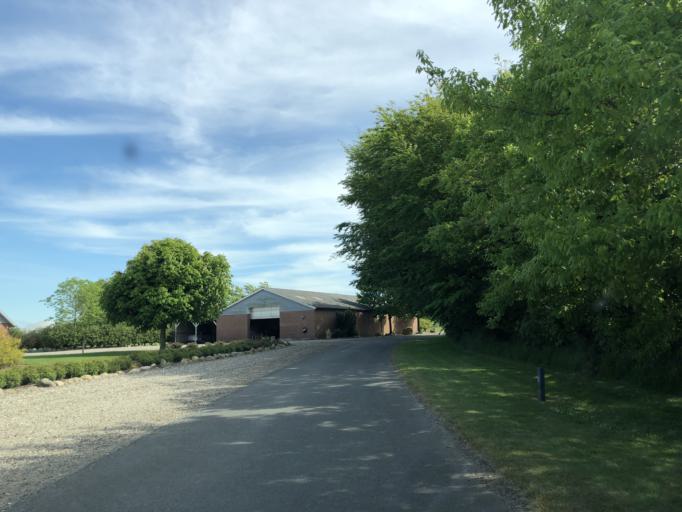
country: DK
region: Central Jutland
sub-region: Holstebro Kommune
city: Ulfborg
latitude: 56.2793
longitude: 8.2682
